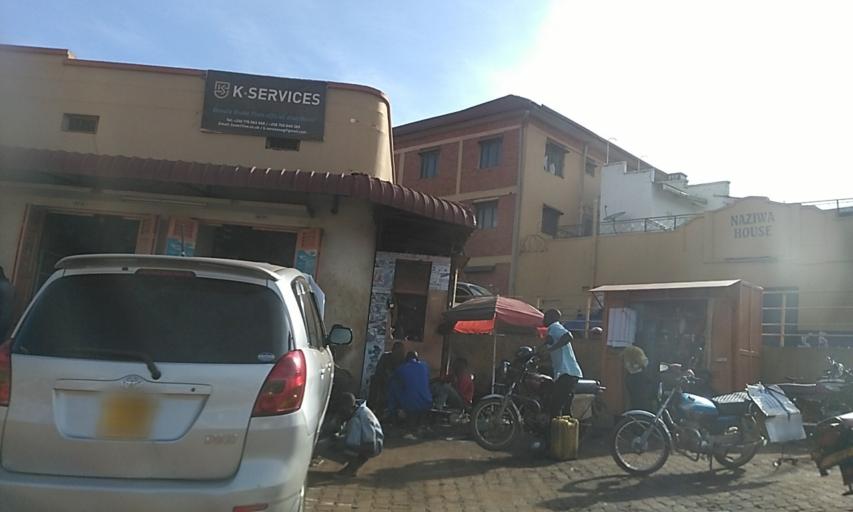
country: UG
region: Central Region
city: Kampala Central Division
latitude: 0.3188
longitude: 32.5699
